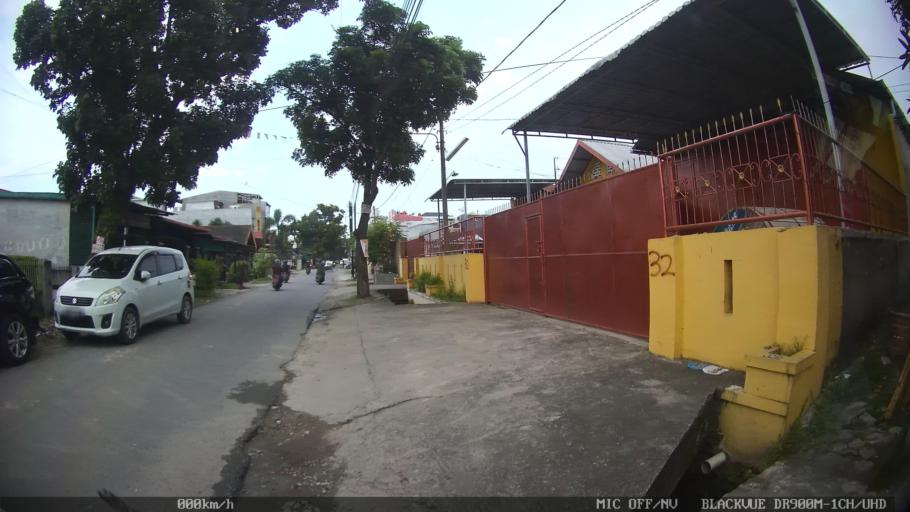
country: ID
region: North Sumatra
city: Medan
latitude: 3.6071
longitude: 98.6972
